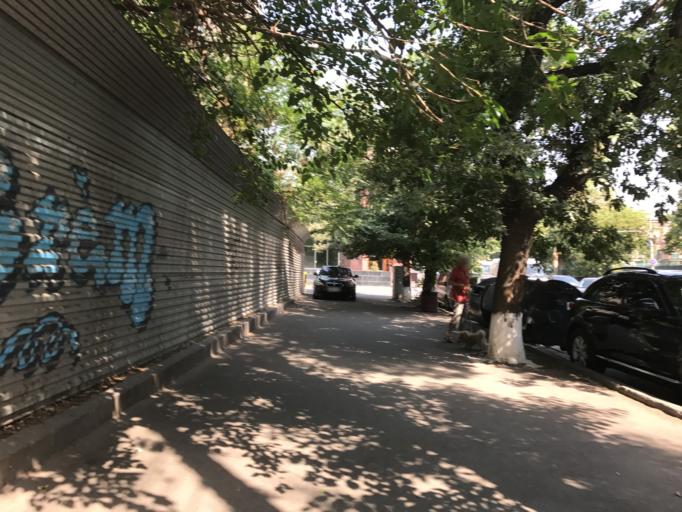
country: AM
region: Yerevan
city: Yerevan
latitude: 40.1729
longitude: 44.5068
